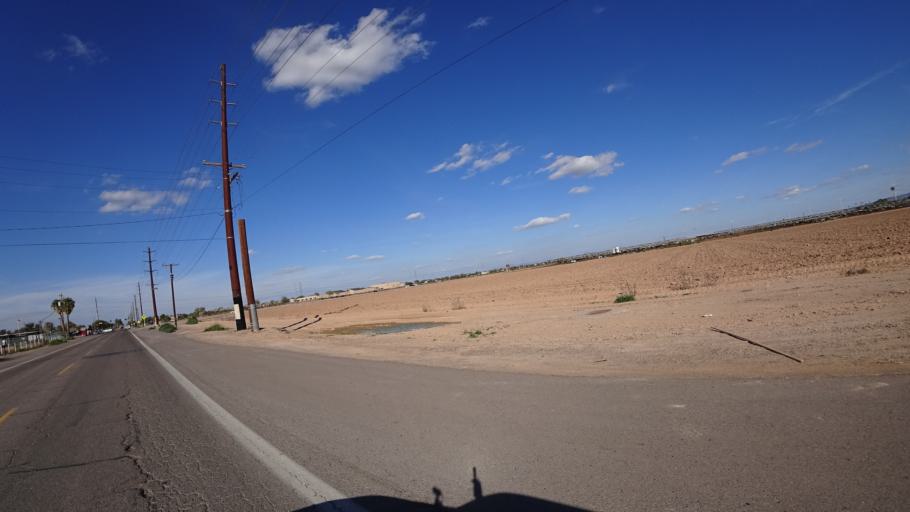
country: US
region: Arizona
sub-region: Maricopa County
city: Tolleson
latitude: 33.4089
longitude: -112.2552
